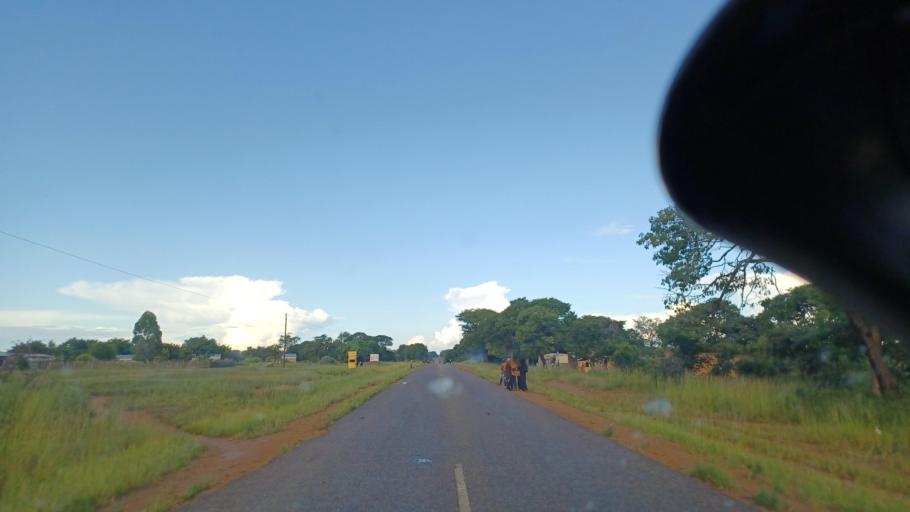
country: ZM
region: North-Western
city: Kalengwa
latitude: -13.2102
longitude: 24.6399
